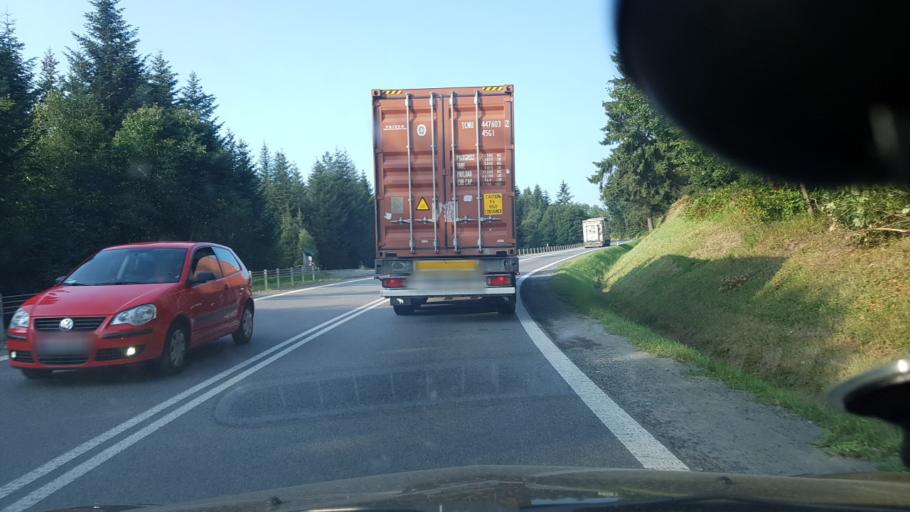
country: PL
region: Lesser Poland Voivodeship
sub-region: Powiat suski
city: Naprawa
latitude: 49.6718
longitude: 19.8994
